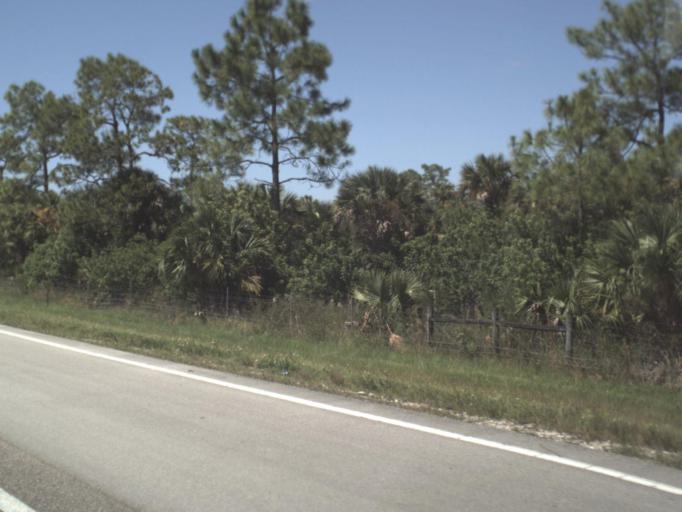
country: US
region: Florida
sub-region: Collier County
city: Orangetree
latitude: 26.1531
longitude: -81.5446
